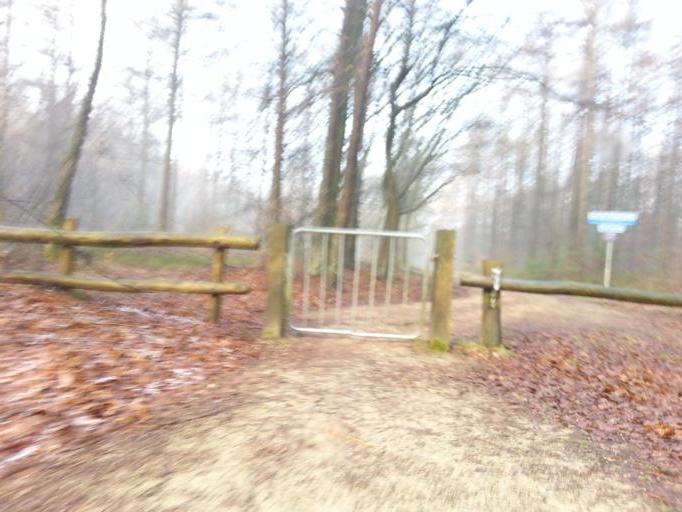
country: NL
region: Utrecht
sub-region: Gemeente Utrechtse Heuvelrug
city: Maarsbergen
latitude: 52.0353
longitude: 5.3964
